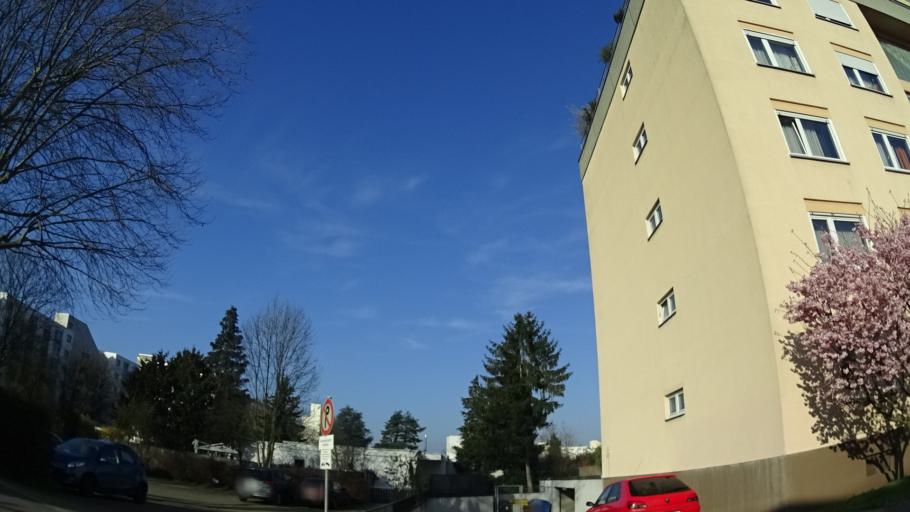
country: DE
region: Baden-Wuerttemberg
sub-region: Karlsruhe Region
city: Leimen
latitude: 49.3742
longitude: 8.6826
